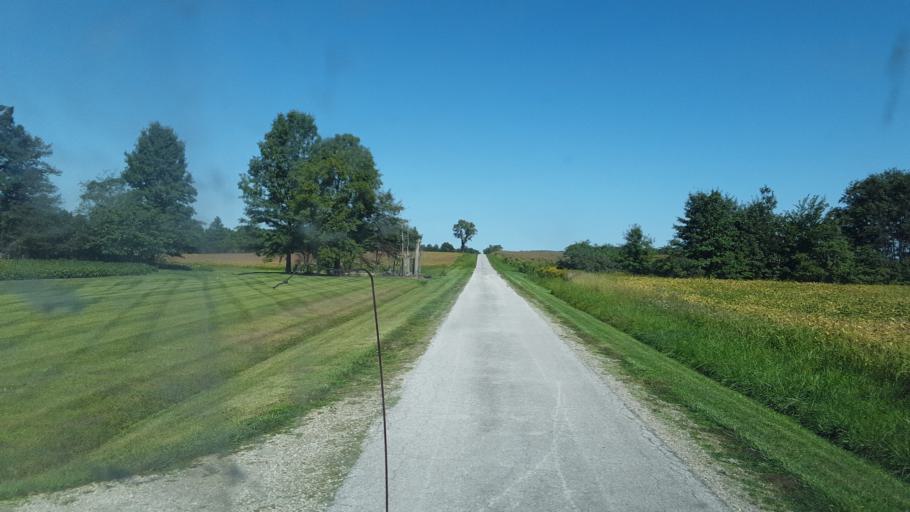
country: US
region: Ohio
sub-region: Sandusky County
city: Mount Carmel
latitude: 41.1530
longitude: -82.9189
